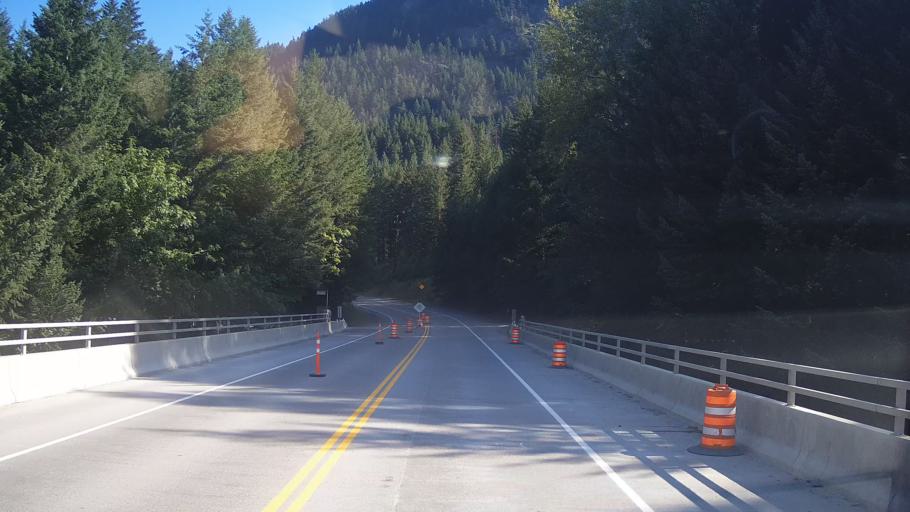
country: CA
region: British Columbia
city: Hope
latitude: 49.7026
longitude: -121.4092
